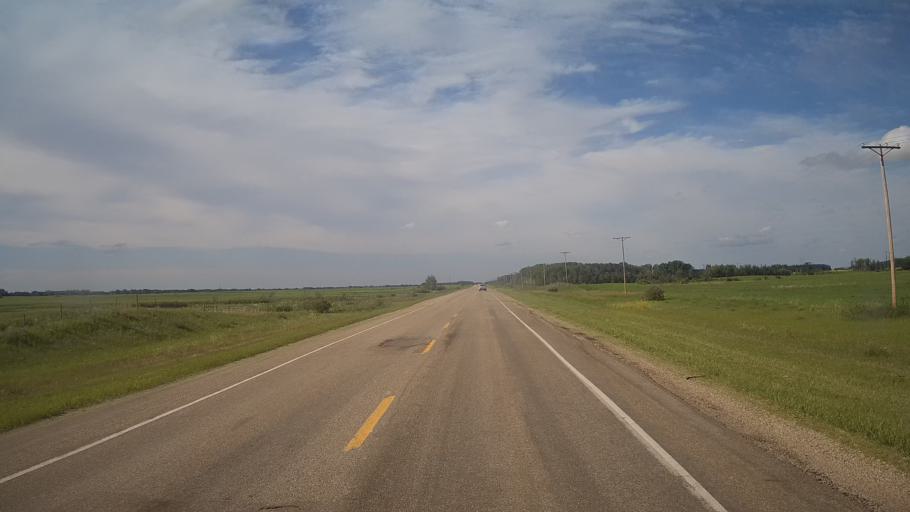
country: CA
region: Saskatchewan
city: Foam Lake
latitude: 51.6168
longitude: -103.8459
